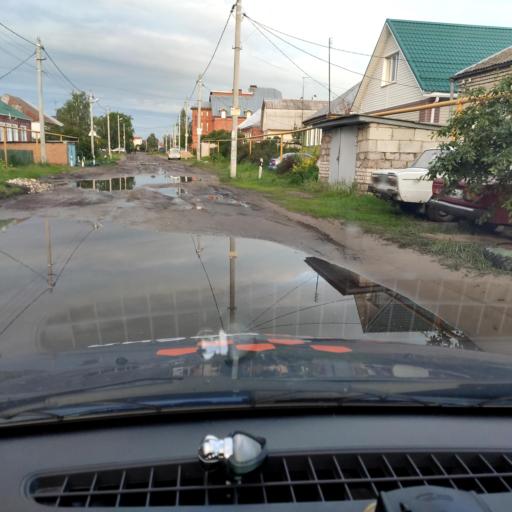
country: RU
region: Voronezj
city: Somovo
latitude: 51.7518
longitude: 39.3292
